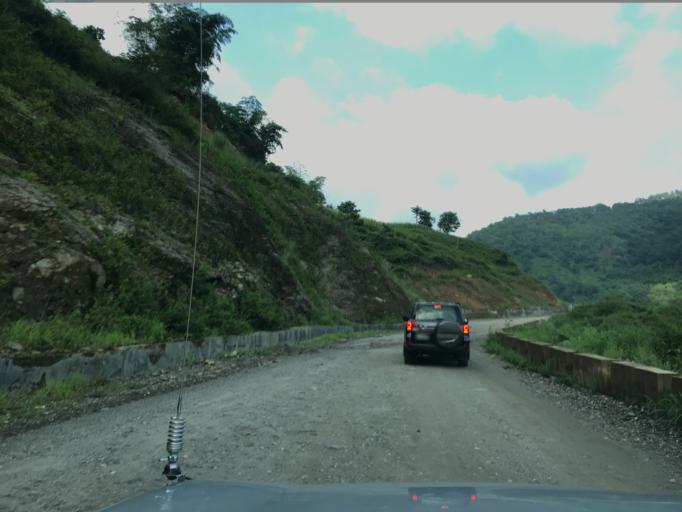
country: TL
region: Dili
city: Dili
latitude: -8.6363
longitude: 125.5126
